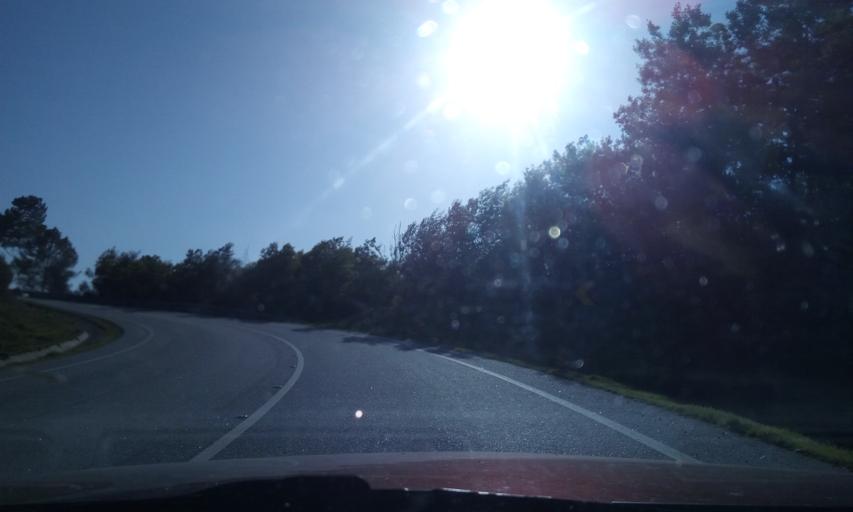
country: PT
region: Guarda
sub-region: Fornos de Algodres
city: Fornos de Algodres
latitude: 40.6172
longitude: -7.5154
